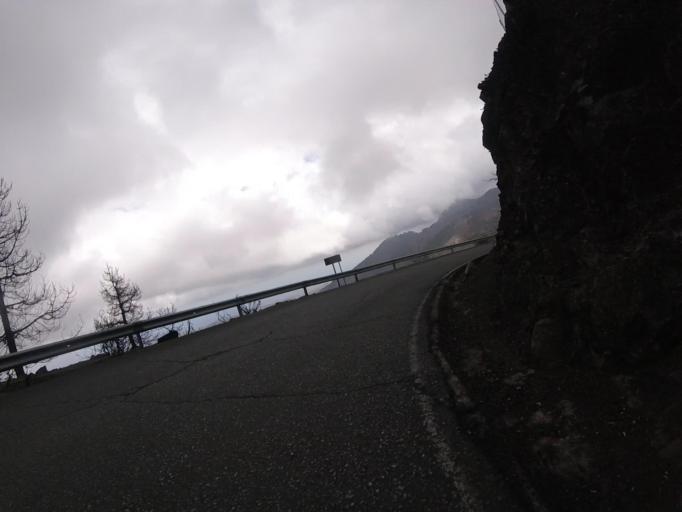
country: ES
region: Canary Islands
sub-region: Provincia de Las Palmas
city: Tejeda
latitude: 27.9898
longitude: -15.5762
